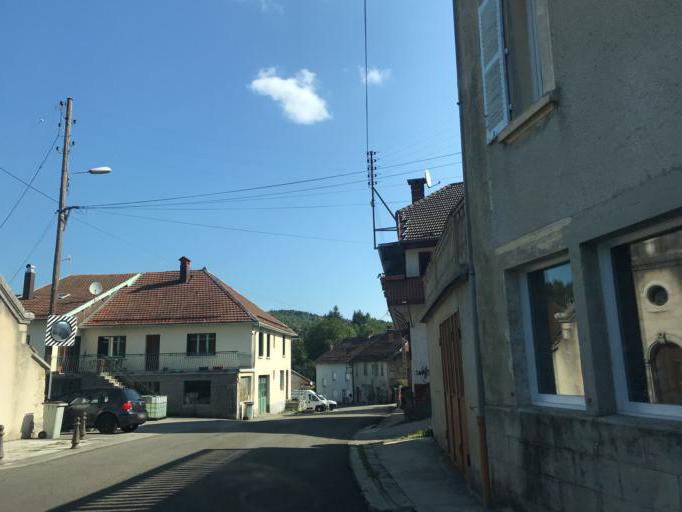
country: FR
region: Franche-Comte
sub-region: Departement du Jura
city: Moirans-en-Montagne
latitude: 46.4133
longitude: 5.7348
